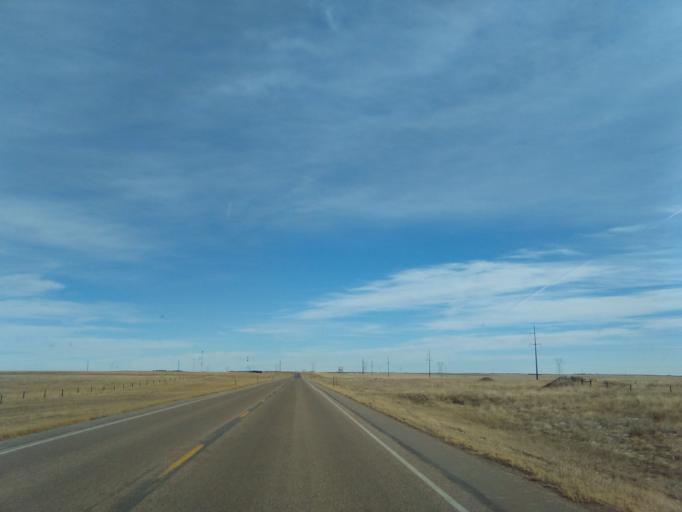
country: US
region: Wyoming
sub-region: Laramie County
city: Pine Bluffs
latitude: 41.4335
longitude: -104.3660
